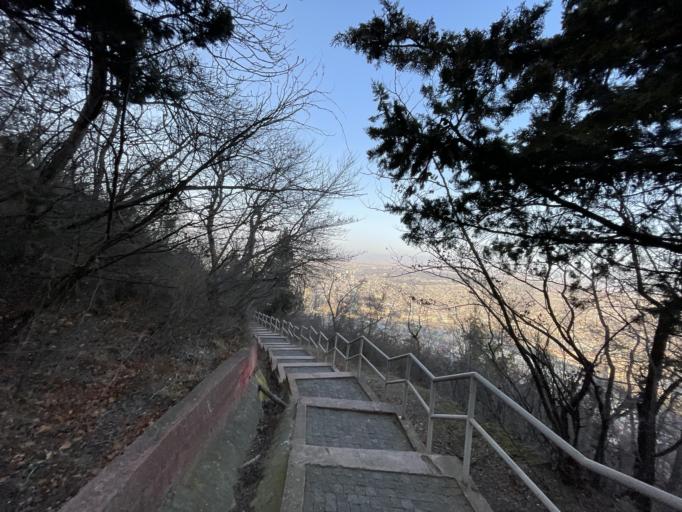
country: GE
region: T'bilisi
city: Tbilisi
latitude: 41.6931
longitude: 44.7885
